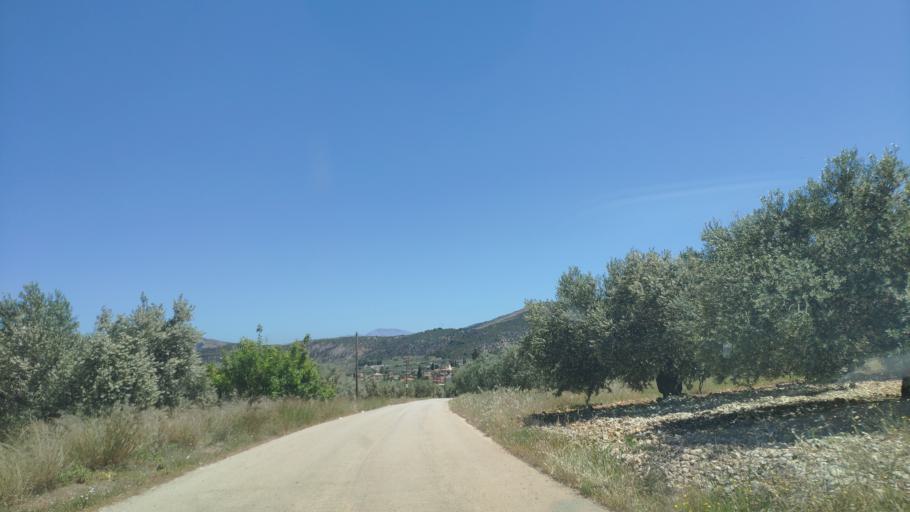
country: GR
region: Peloponnese
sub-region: Nomos Korinthias
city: Athikia
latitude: 37.8111
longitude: 22.9188
